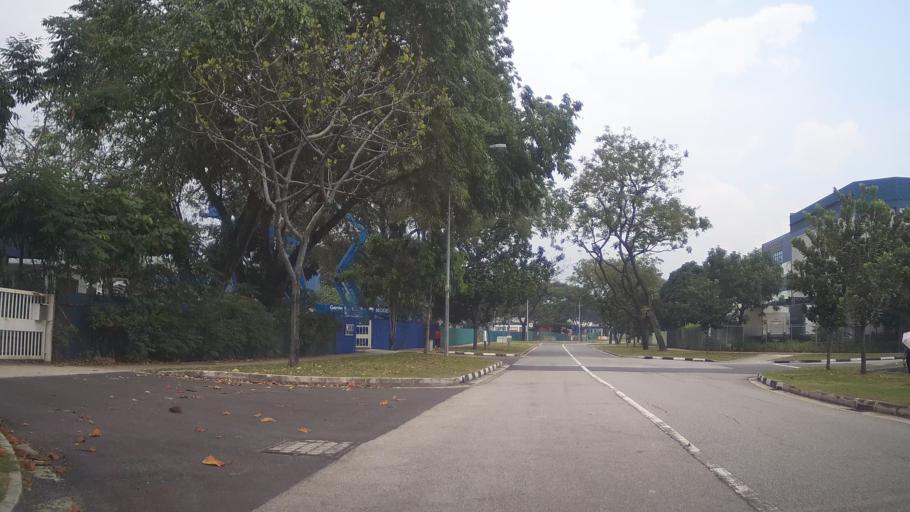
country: MY
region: Johor
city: Johor Bahru
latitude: 1.3333
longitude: 103.7051
